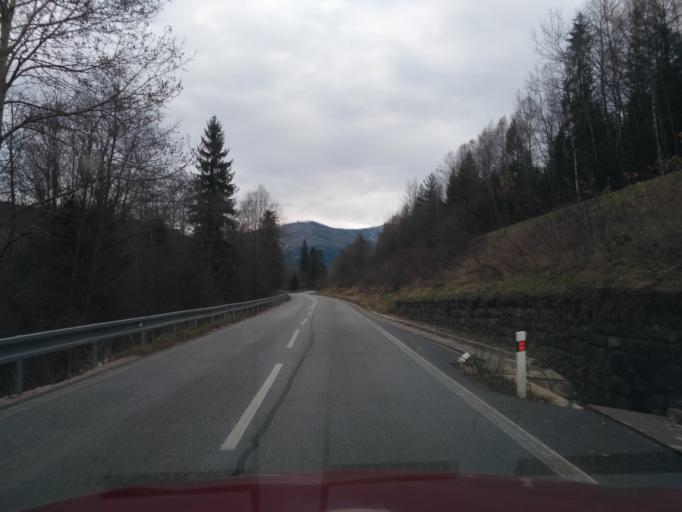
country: SK
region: Kosicky
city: Spisska Nova Ves
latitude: 48.8291
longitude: 20.6511
